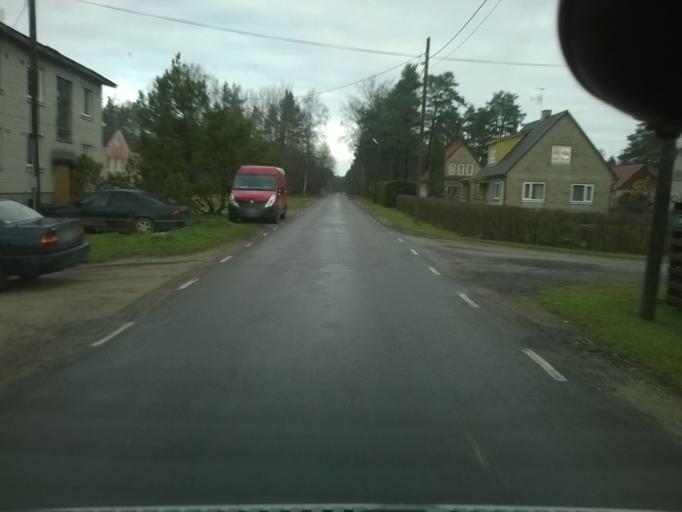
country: EE
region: Laeaene
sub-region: Ridala Parish
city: Uuemoisa
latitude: 58.9511
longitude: 23.7252
